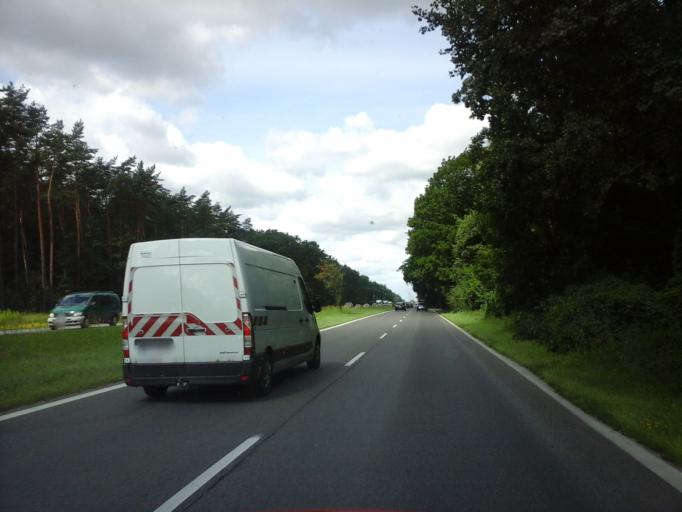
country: PL
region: West Pomeranian Voivodeship
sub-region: Powiat gryfinski
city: Stare Czarnowo
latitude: 53.3676
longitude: 14.7239
